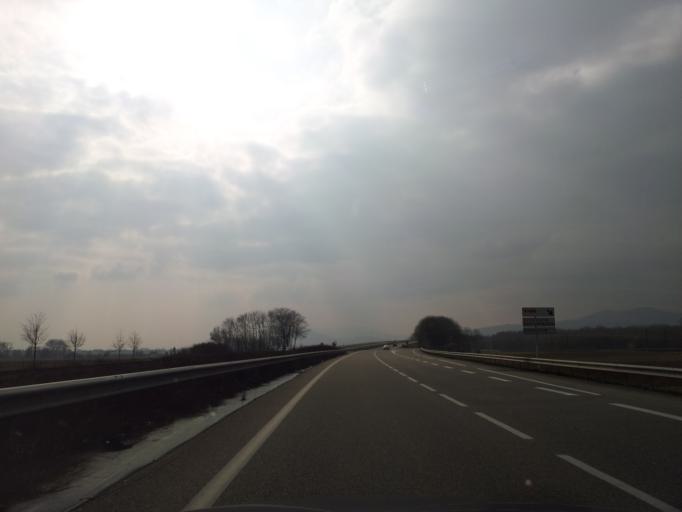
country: FR
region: Alsace
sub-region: Departement du Bas-Rhin
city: Ebersheim
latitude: 48.3243
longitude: 7.5182
